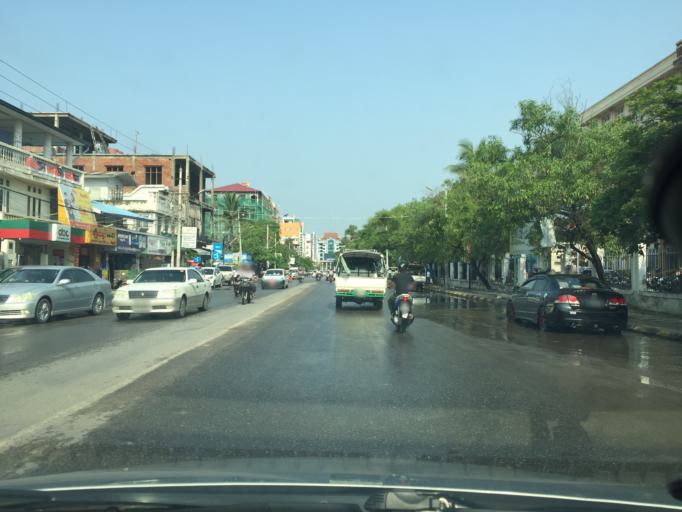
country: MM
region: Mandalay
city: Mandalay
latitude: 21.9766
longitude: 96.0926
